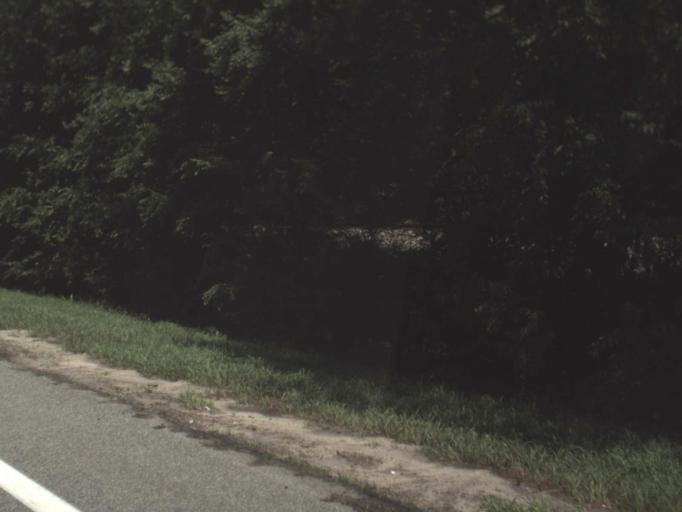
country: US
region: Florida
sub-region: Suwannee County
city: Live Oak
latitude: 30.3597
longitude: -83.1259
